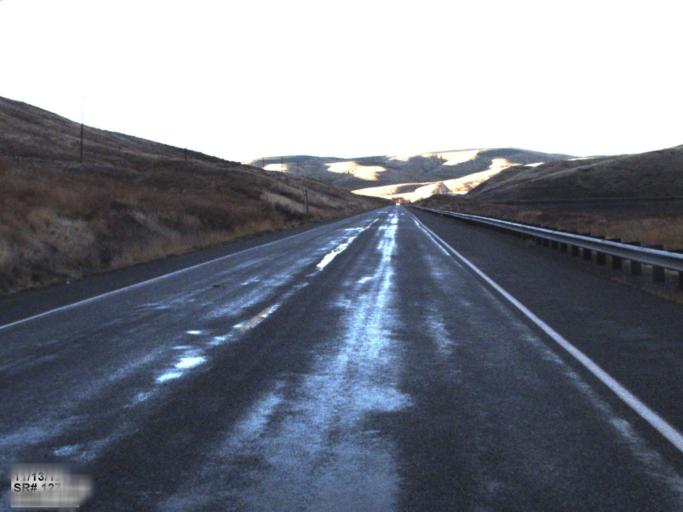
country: US
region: Washington
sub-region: Garfield County
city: Pomeroy
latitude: 46.6067
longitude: -117.7863
